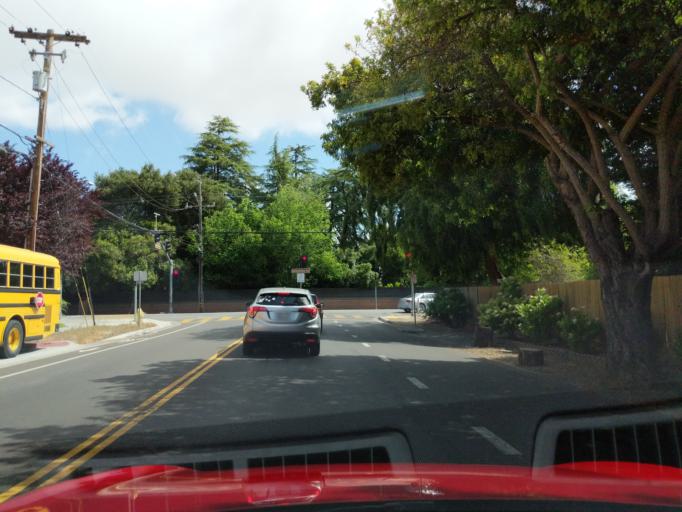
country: US
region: California
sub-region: San Mateo County
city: Menlo Park
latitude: 37.4647
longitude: -122.1851
